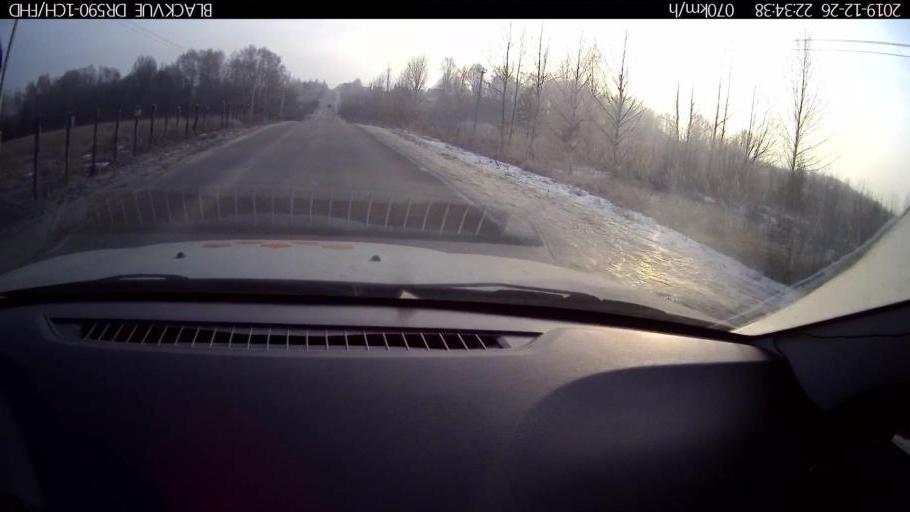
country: RU
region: Nizjnij Novgorod
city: Burevestnik
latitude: 56.1547
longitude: 43.7113
